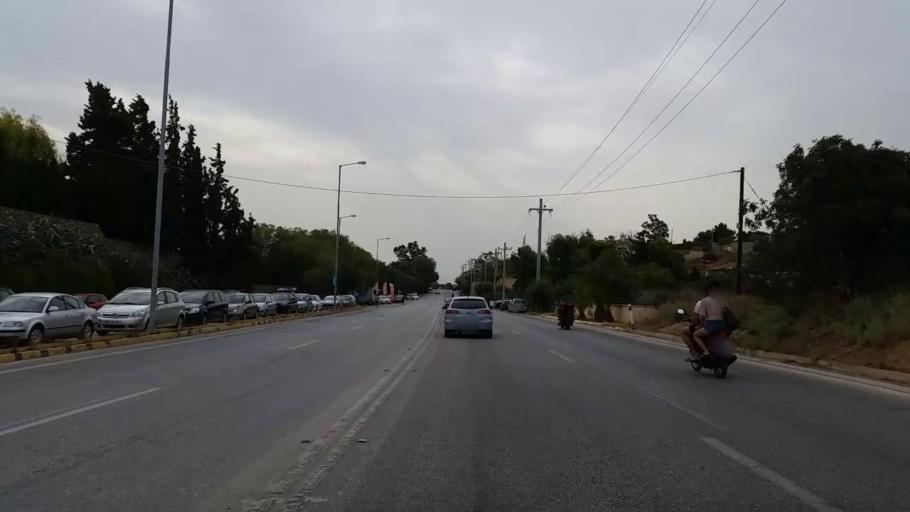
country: GR
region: Attica
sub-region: Nomarchia Anatolikis Attikis
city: Agios Dimitrios Kropias
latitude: 37.7923
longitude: 23.8788
